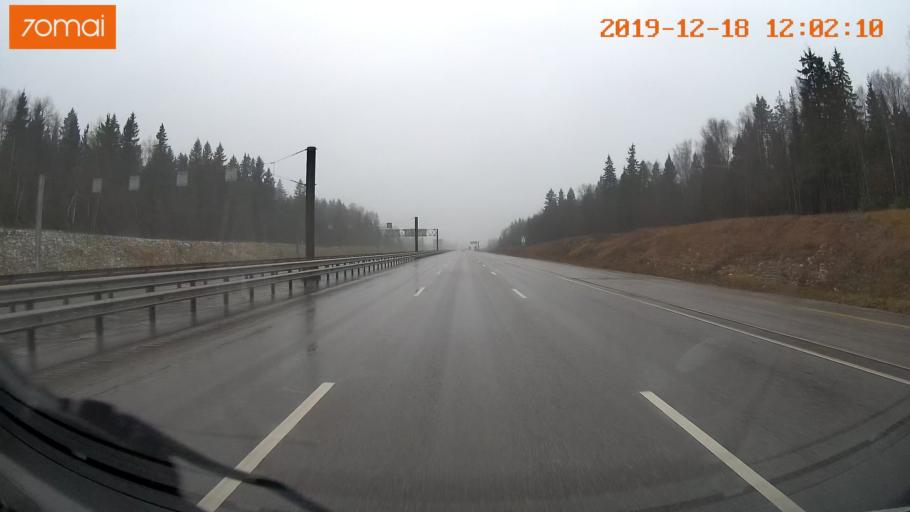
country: RU
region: Moskovskaya
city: Kostrovo
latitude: 55.8540
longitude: 36.7773
